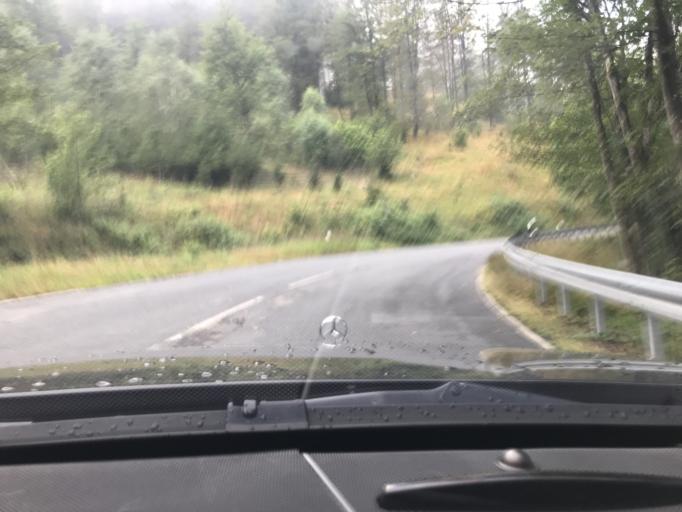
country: DE
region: Lower Saxony
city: Sankt Andreasberg
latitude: 51.6948
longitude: 10.5646
